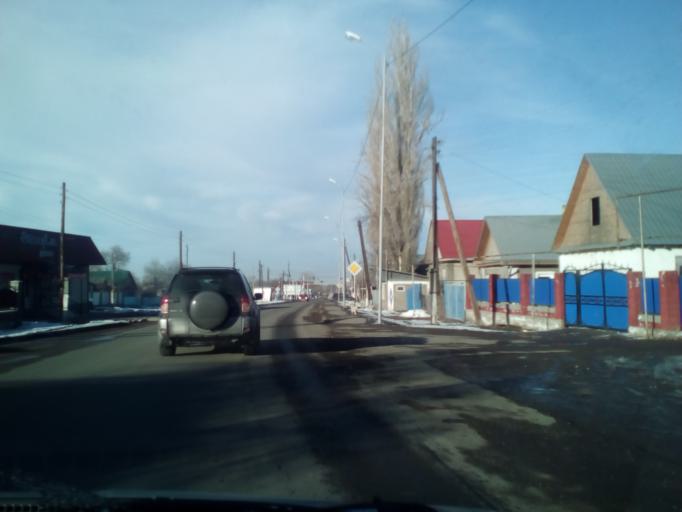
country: KZ
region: Almaty Oblysy
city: Burunday
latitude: 43.1768
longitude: 76.4145
